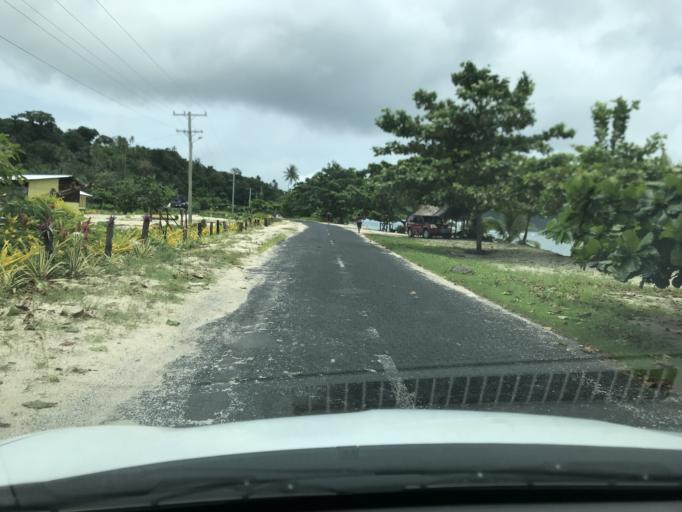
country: WS
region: Va`a-o-Fonoti
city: Samamea
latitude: -14.0455
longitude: -171.4505
